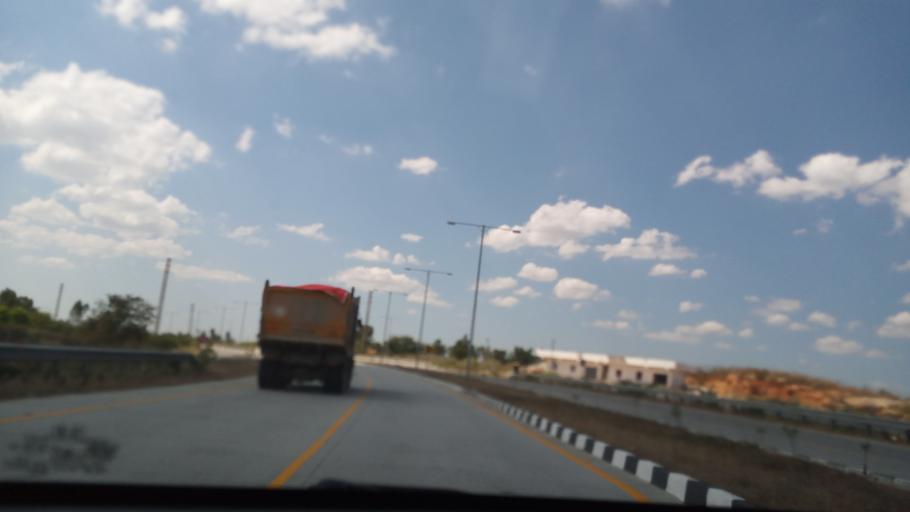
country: IN
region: Andhra Pradesh
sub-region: Chittoor
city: Palmaner
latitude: 13.2197
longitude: 78.7429
